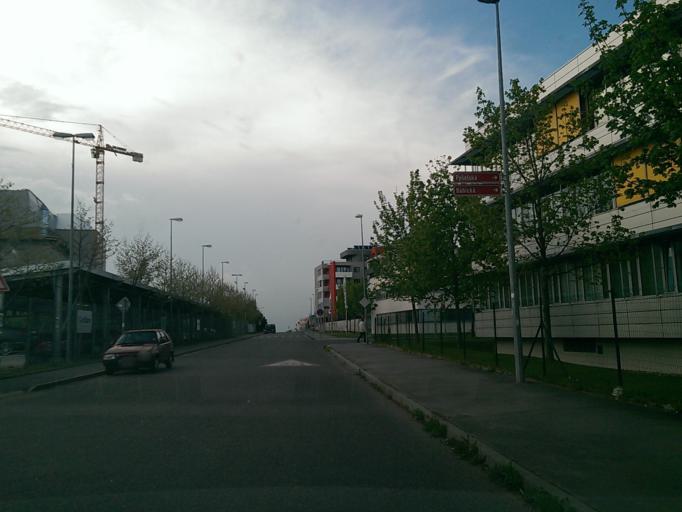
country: CZ
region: Central Bohemia
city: Vestec
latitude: 50.0384
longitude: 14.4974
